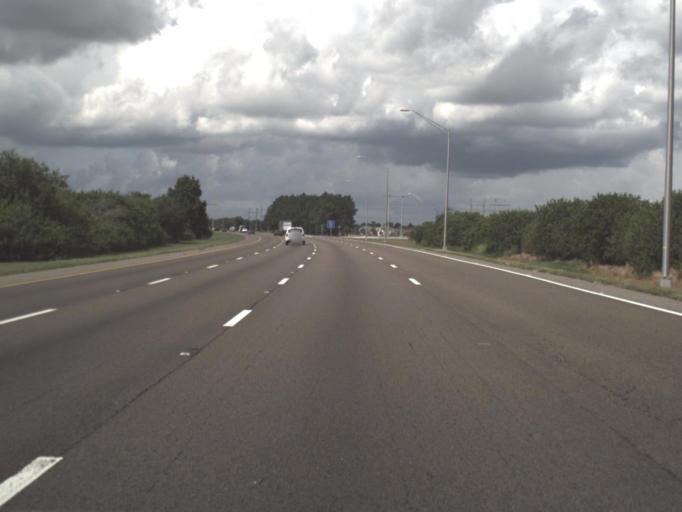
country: US
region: Florida
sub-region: Hillsborough County
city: Ruskin
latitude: 27.6914
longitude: -82.4162
